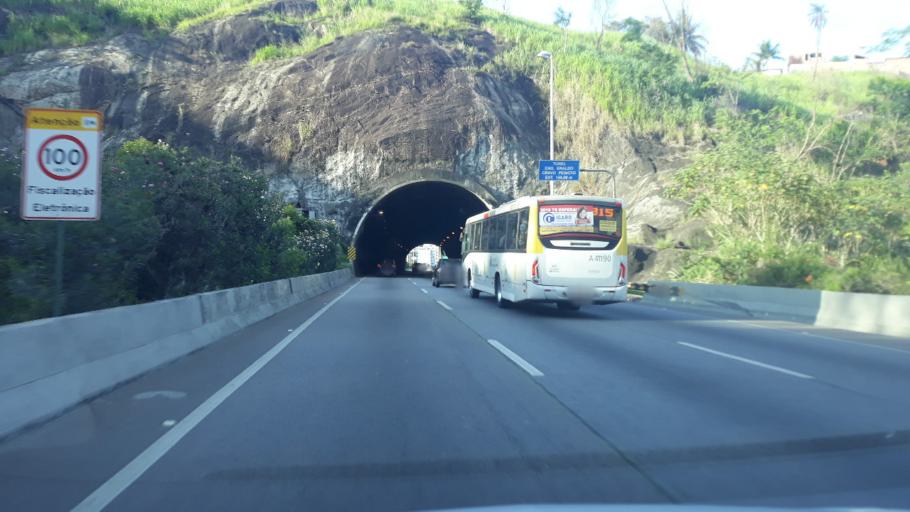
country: BR
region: Rio de Janeiro
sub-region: Sao Joao De Meriti
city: Sao Joao de Meriti
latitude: -22.9328
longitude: -43.3453
